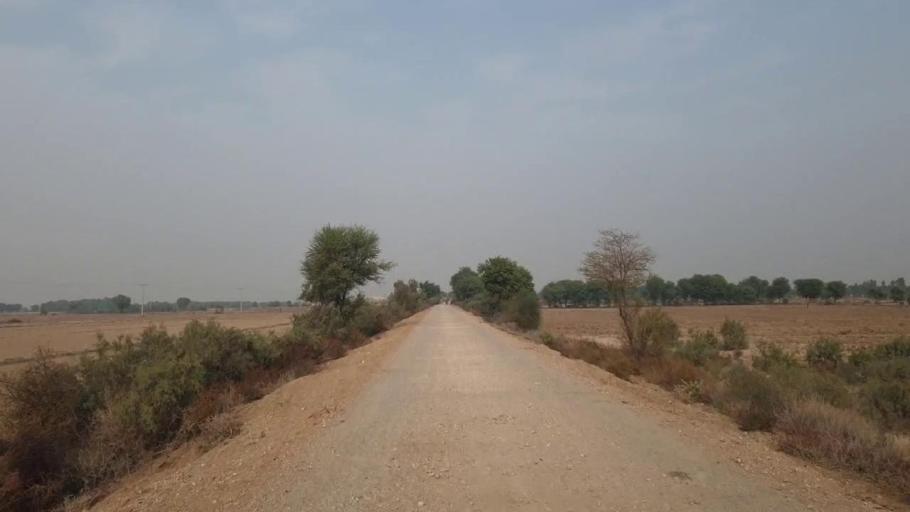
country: PK
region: Sindh
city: Sann
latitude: 26.1044
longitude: 68.0801
